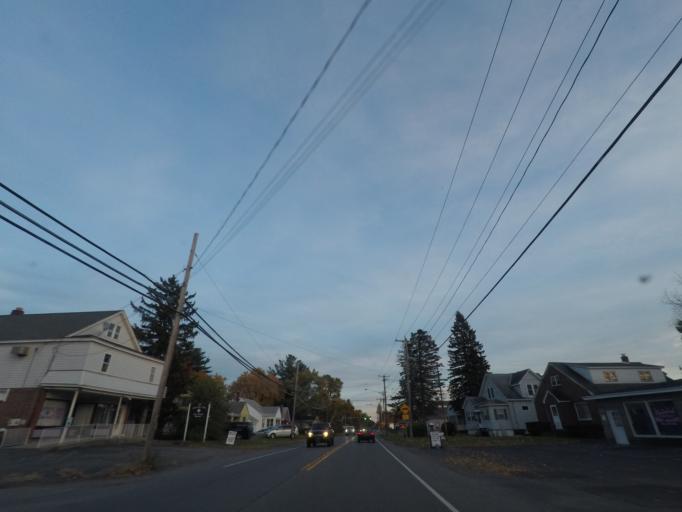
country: US
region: New York
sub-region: Schenectady County
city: Rotterdam
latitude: 42.7848
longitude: -73.9656
